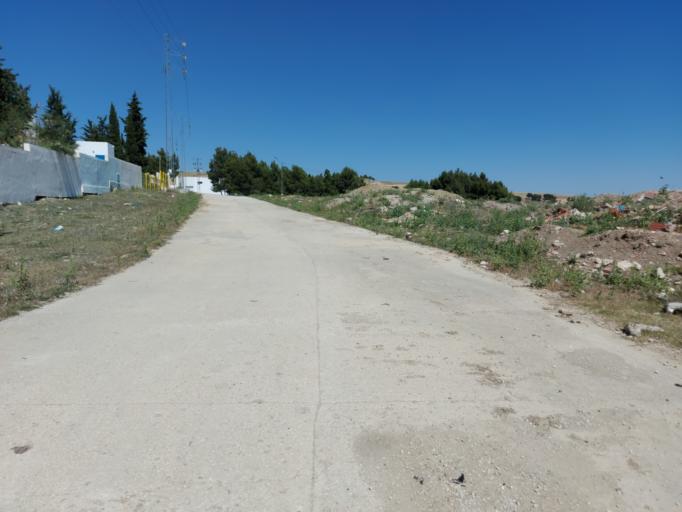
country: TN
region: Kef
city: El Kef
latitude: 36.1833
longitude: 8.7271
